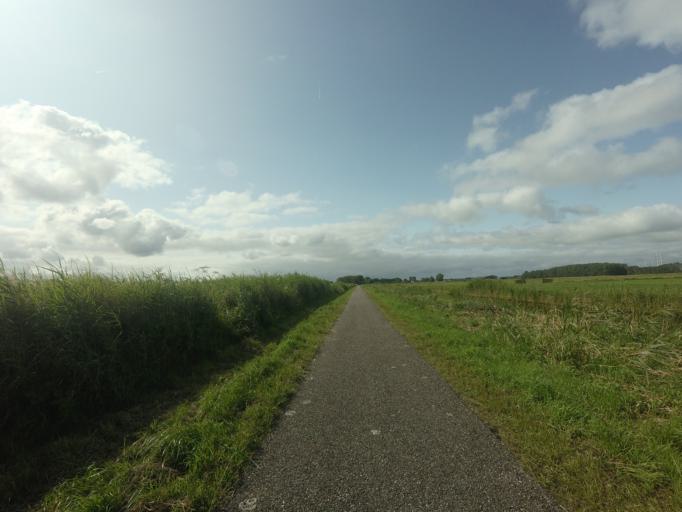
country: NL
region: North Holland
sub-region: Gemeente Haarlem
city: Haarlem
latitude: 52.3961
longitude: 4.7016
